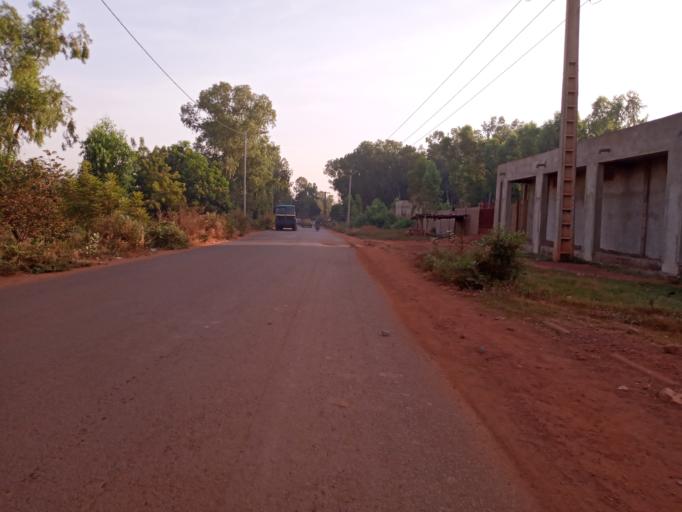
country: ML
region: Bamako
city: Bamako
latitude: 12.6298
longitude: -7.9452
